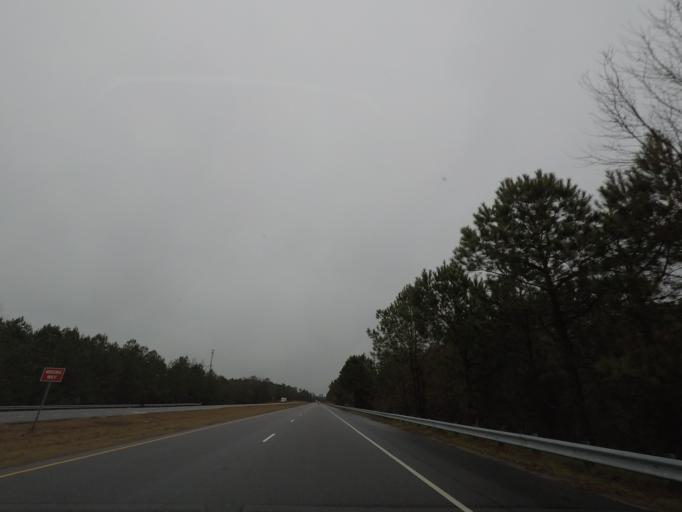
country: US
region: North Carolina
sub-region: Lee County
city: Broadway
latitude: 35.3393
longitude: -79.0997
